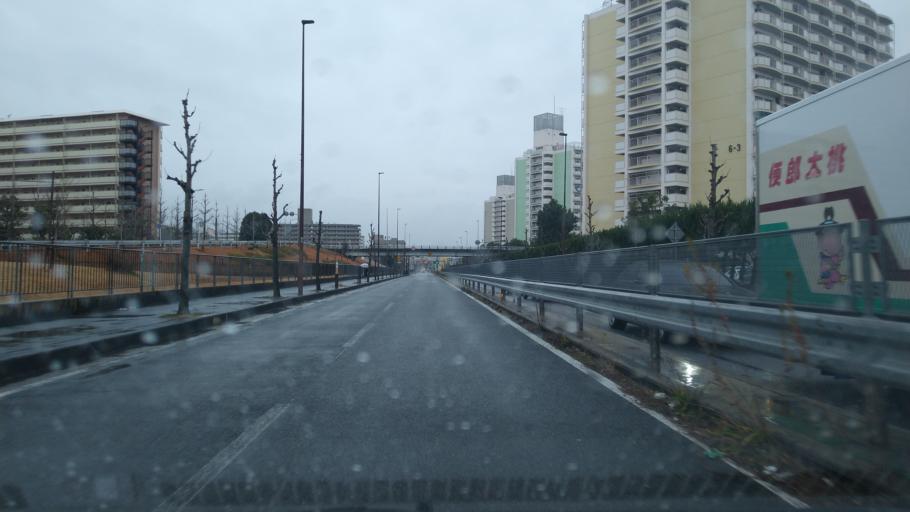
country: JP
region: Kyoto
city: Uji
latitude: 34.9206
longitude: 135.7755
